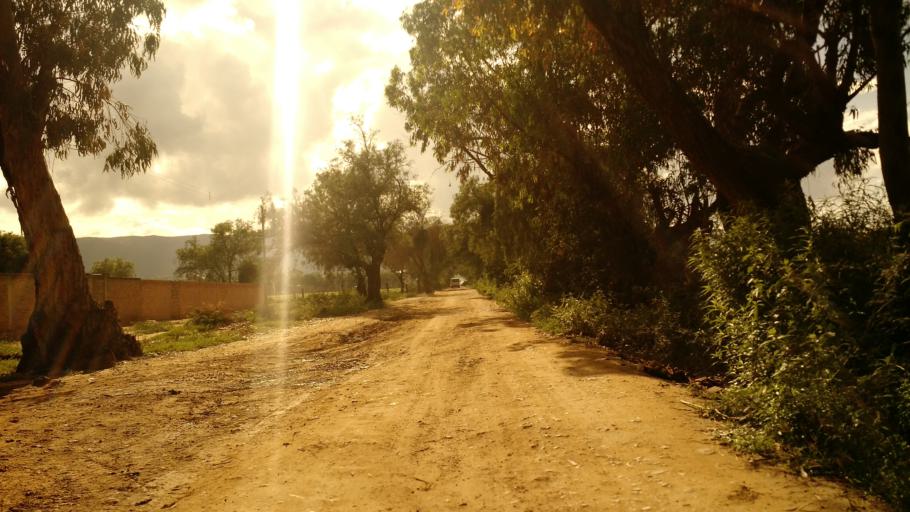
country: BO
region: Cochabamba
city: Cochabamba
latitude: -17.4552
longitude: -66.1456
